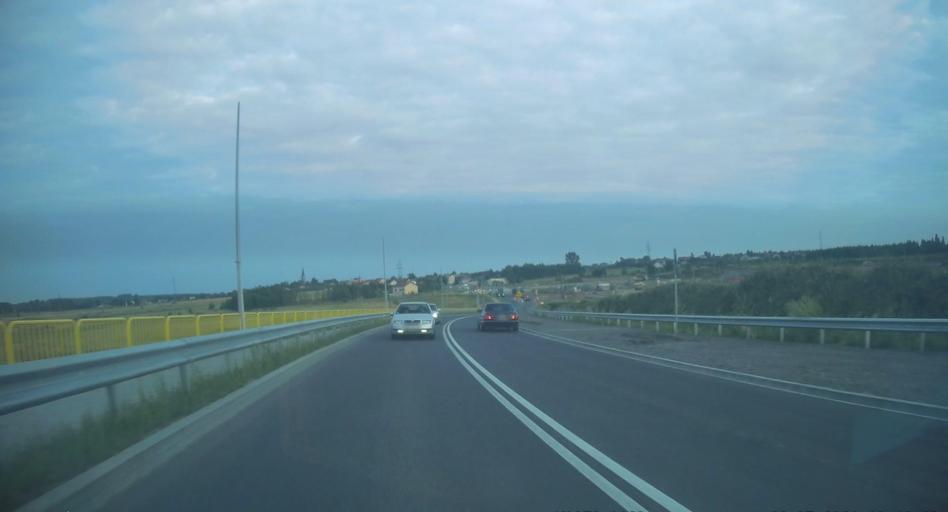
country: PL
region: Lodz Voivodeship
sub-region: Powiat radomszczanski
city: Kamiensk
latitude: 51.2110
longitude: 19.4890
